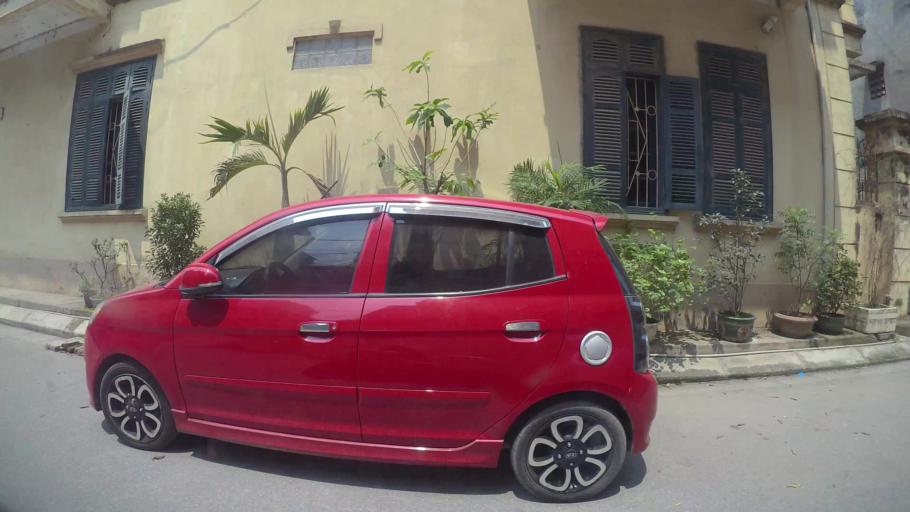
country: VN
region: Ha Noi
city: Thanh Xuan
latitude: 20.9964
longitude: 105.7854
